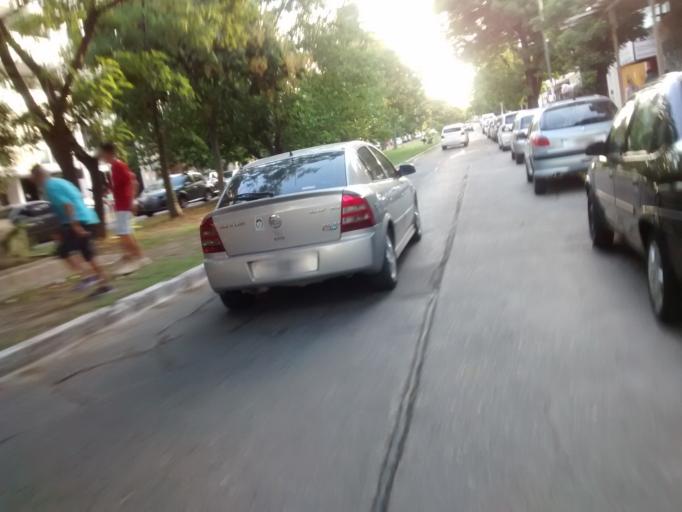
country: AR
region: Buenos Aires
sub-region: Partido de La Plata
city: La Plata
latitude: -34.9113
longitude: -57.9684
